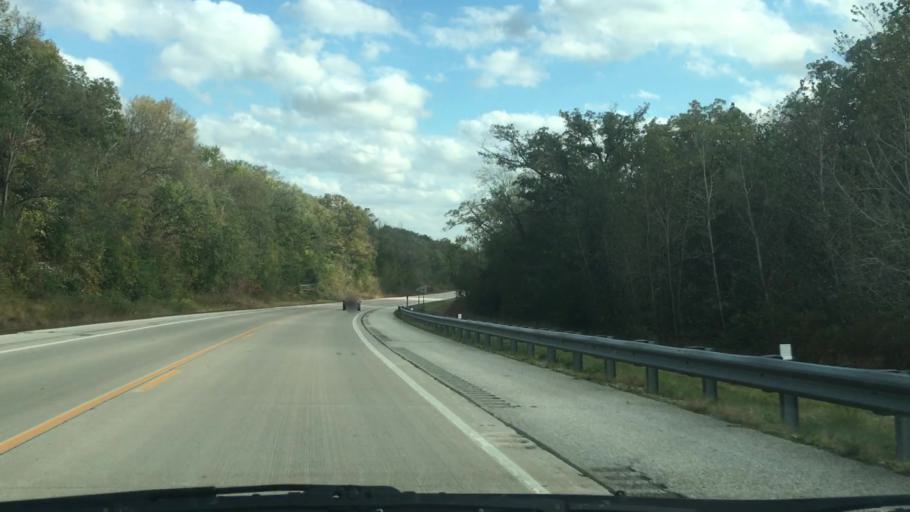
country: US
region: Minnesota
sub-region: Fillmore County
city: Preston
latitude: 43.7266
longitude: -92.1302
